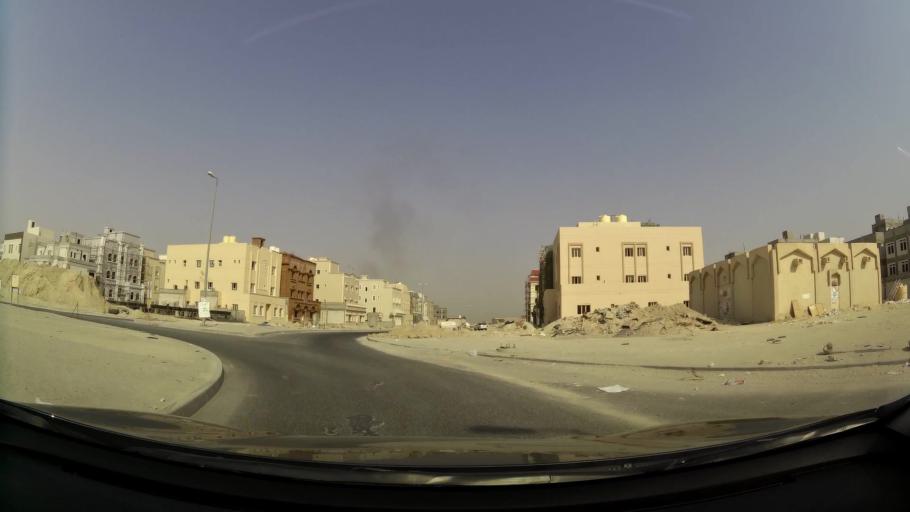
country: KW
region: Muhafazat al Jahra'
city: Al Jahra'
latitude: 29.3502
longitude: 47.7455
